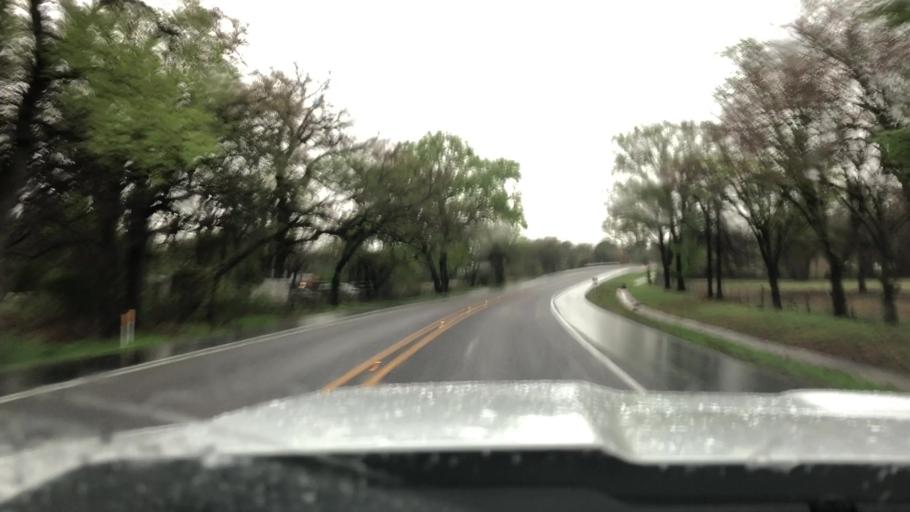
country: US
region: Texas
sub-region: Johnson County
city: Keene
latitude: 32.4478
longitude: -97.3075
